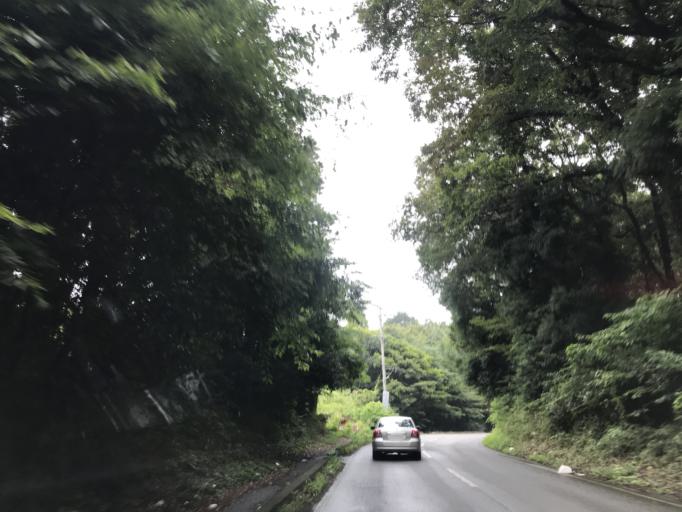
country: JP
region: Ibaraki
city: Sakai
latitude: 36.1500
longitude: 139.7882
